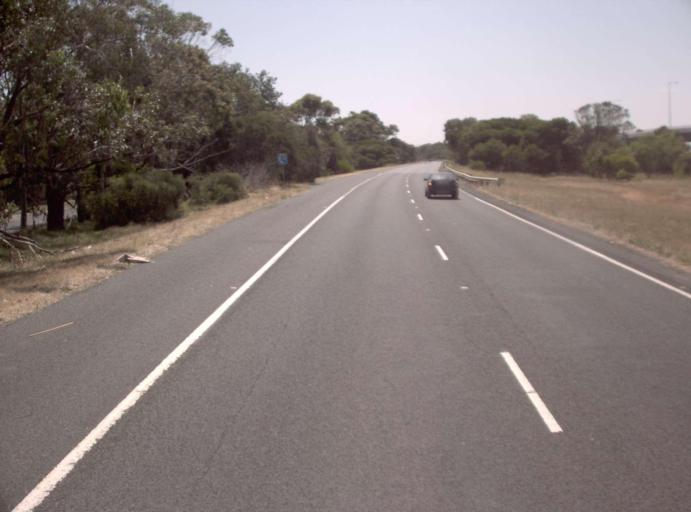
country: AU
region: Victoria
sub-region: Frankston
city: Seaford
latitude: -38.0977
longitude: 145.1441
